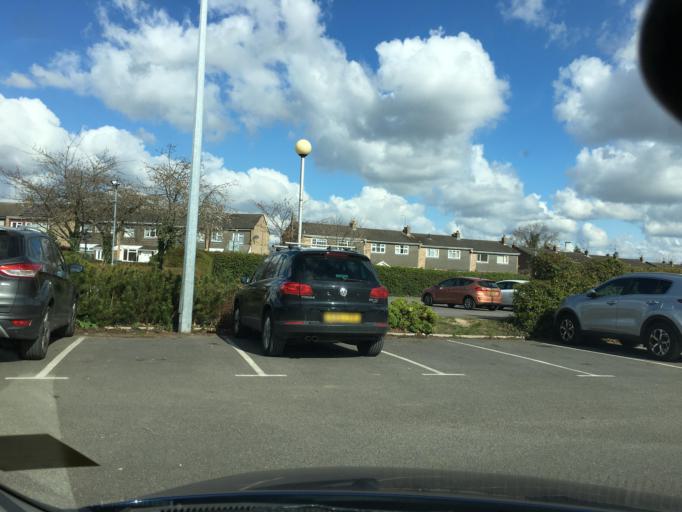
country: GB
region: England
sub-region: Hampshire
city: Yateley
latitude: 51.3376
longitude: -0.8385
